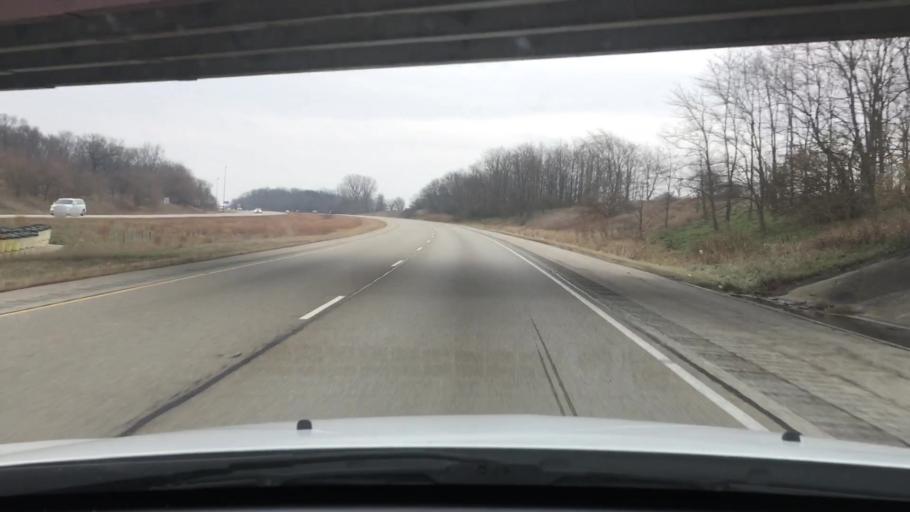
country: US
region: Illinois
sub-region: McLean County
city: Twin Grove
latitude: 40.3534
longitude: -89.1141
